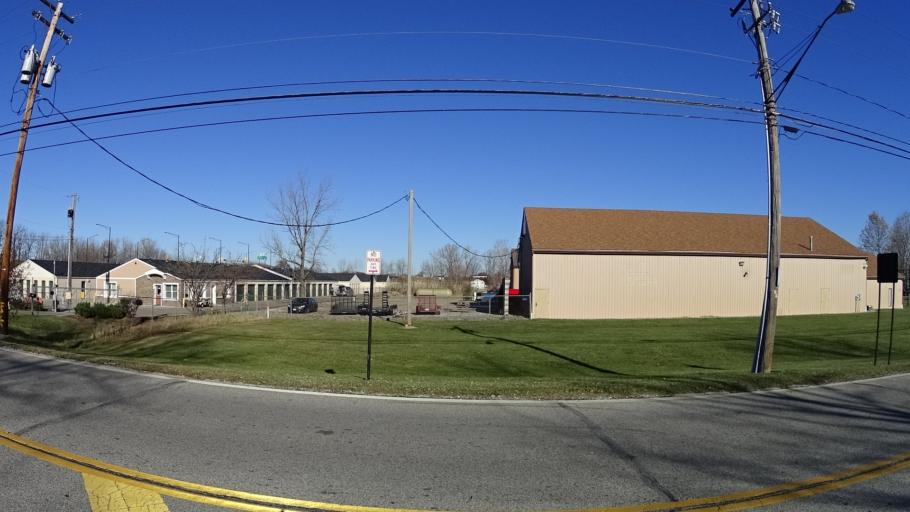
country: US
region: Ohio
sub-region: Lorain County
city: Elyria
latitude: 41.3716
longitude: -82.0744
